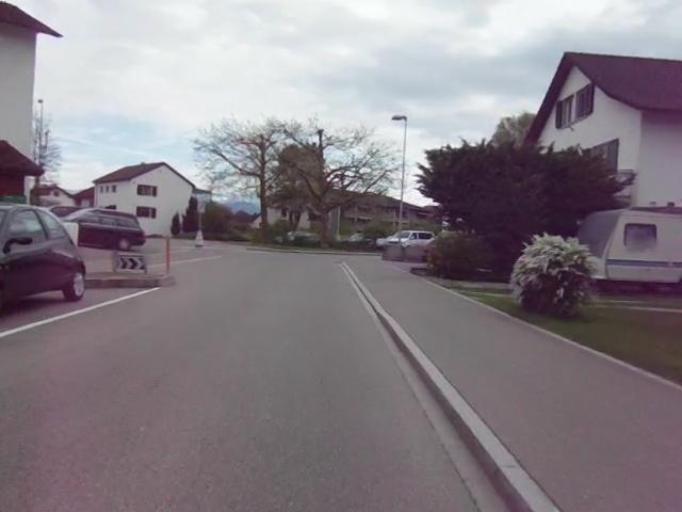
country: CH
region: Zurich
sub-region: Bezirk Hinwil
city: Rueti / Westlicher Dorfteil
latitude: 47.2527
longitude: 8.8426
